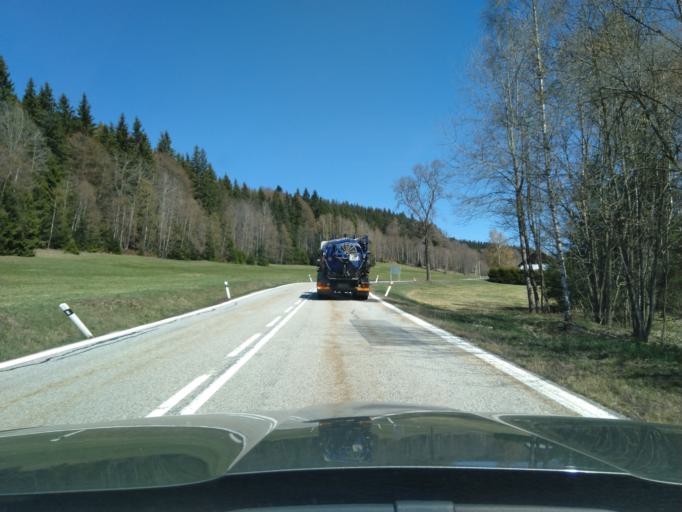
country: CZ
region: Jihocesky
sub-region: Okres Prachatice
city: Vimperk
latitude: 48.9748
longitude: 13.7625
